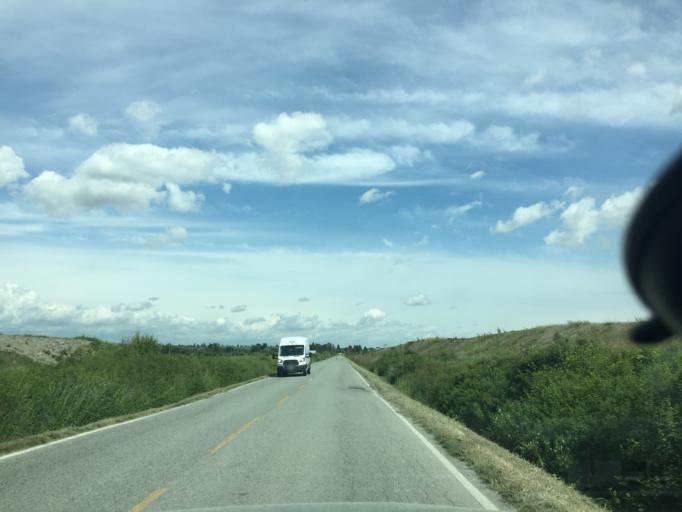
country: CA
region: British Columbia
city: Richmond
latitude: 49.2066
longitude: -123.1887
